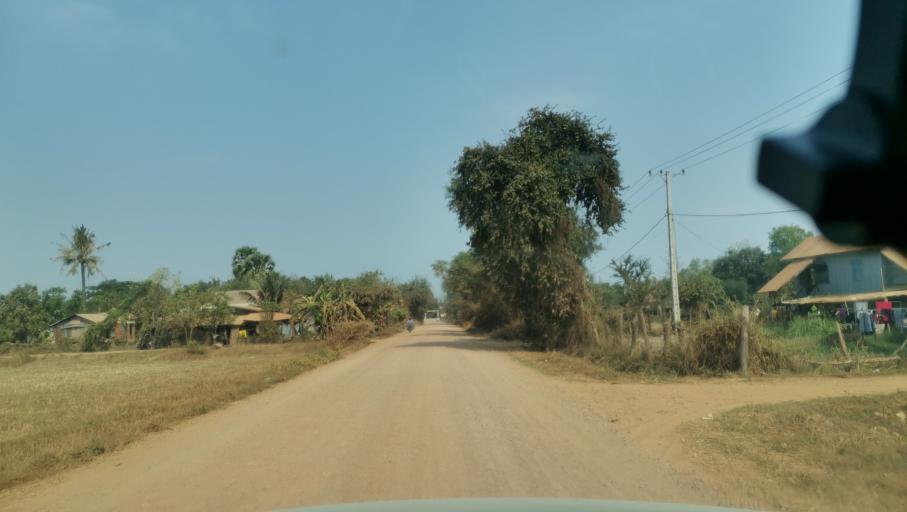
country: KH
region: Battambang
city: Battambang
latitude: 13.0700
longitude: 103.1694
